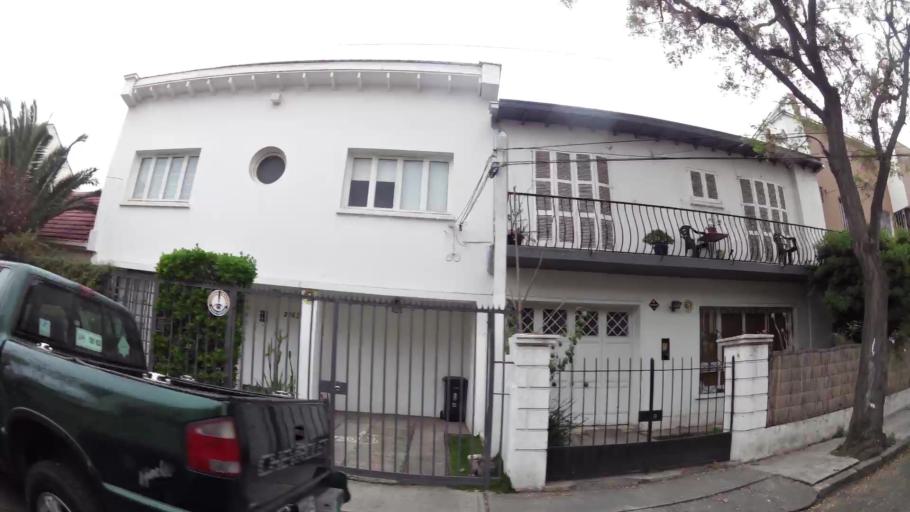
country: CL
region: Santiago Metropolitan
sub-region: Provincia de Santiago
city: Santiago
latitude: -33.4506
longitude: -70.6155
